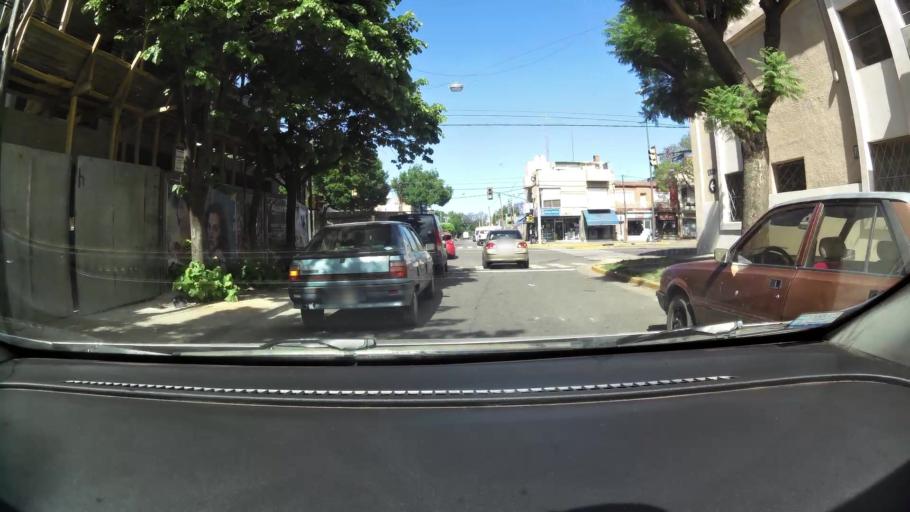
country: AR
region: Santa Fe
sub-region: Departamento de Rosario
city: Rosario
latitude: -32.9391
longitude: -60.7130
